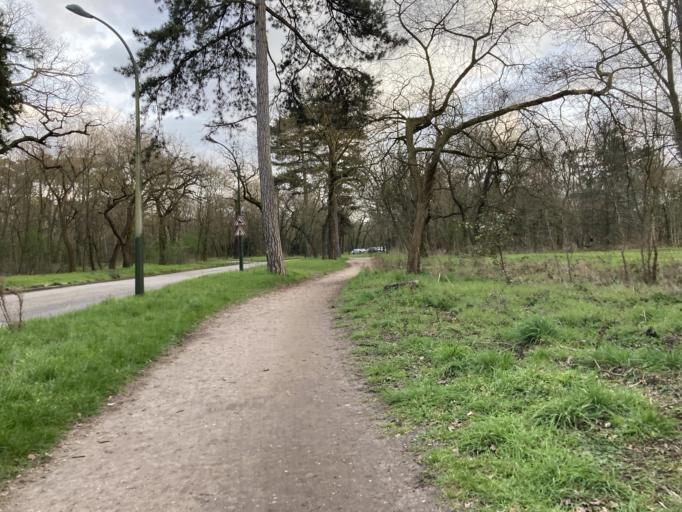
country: FR
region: Ile-de-France
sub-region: Departement des Hauts-de-Seine
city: Neuilly-sur-Seine
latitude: 48.8754
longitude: 2.2627
